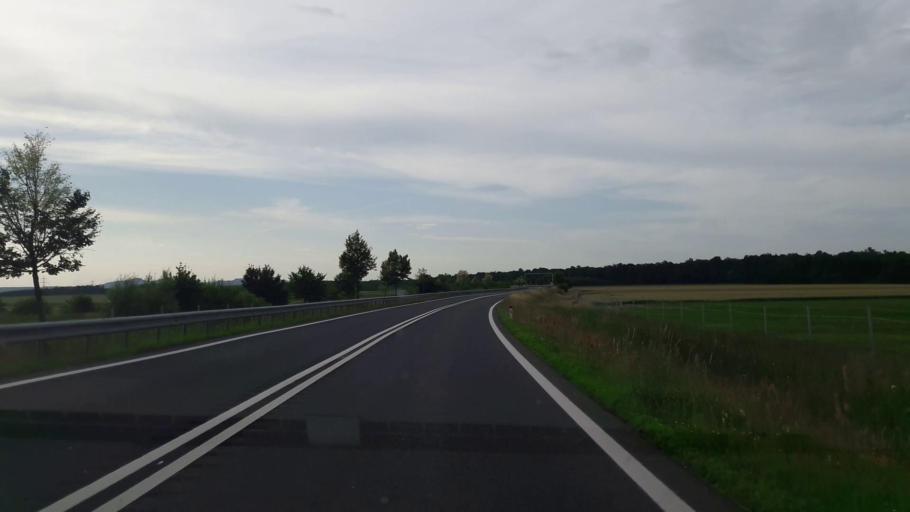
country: AT
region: Burgenland
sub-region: Politischer Bezirk Oberpullendorf
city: Oberpullendorf
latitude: 47.4974
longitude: 16.4864
